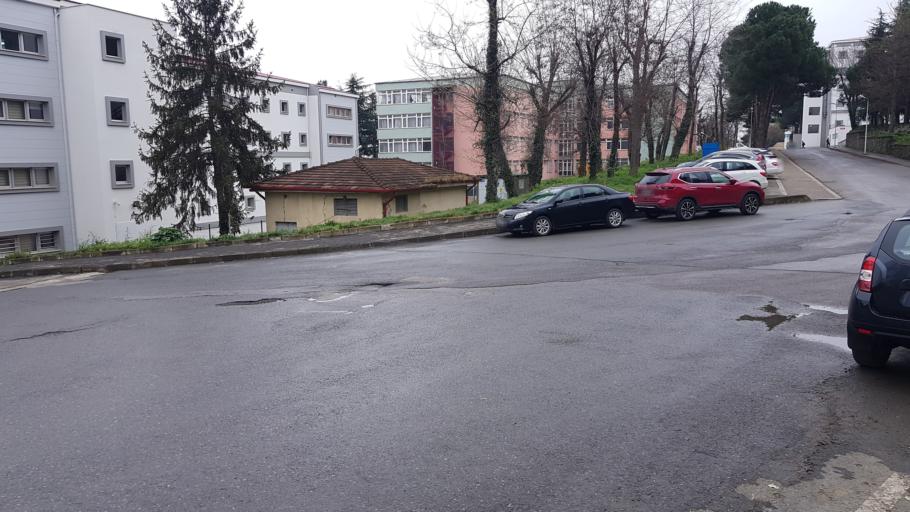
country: TR
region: Trabzon
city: Trabzon
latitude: 40.9949
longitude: 39.7676
